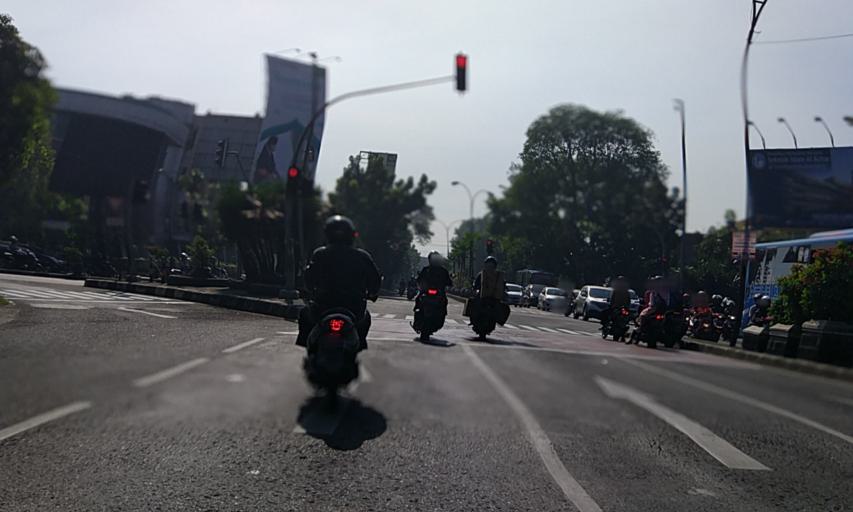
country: ID
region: West Java
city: Bandung
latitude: -6.9159
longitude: 107.6296
